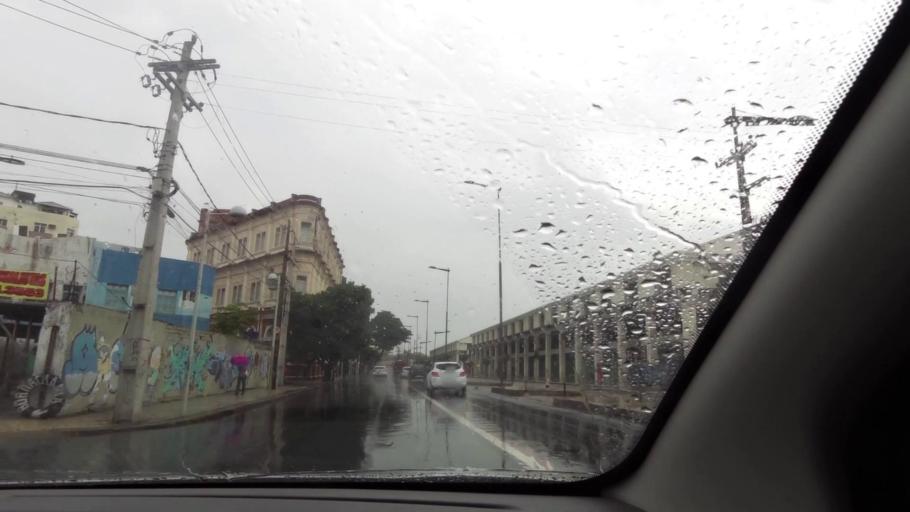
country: BR
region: Pernambuco
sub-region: Recife
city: Recife
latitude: -8.0651
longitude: -34.8723
